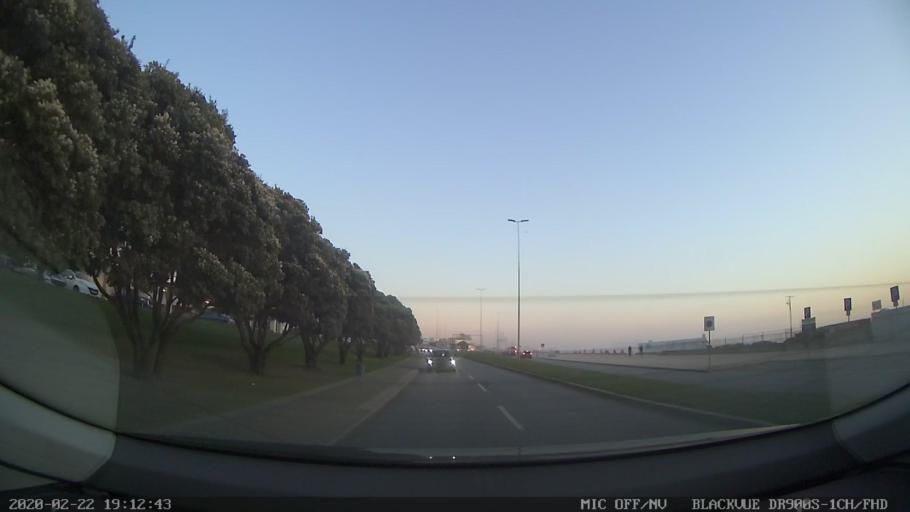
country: PT
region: Porto
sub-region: Matosinhos
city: Leca da Palmeira
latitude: 41.1934
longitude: -8.7069
